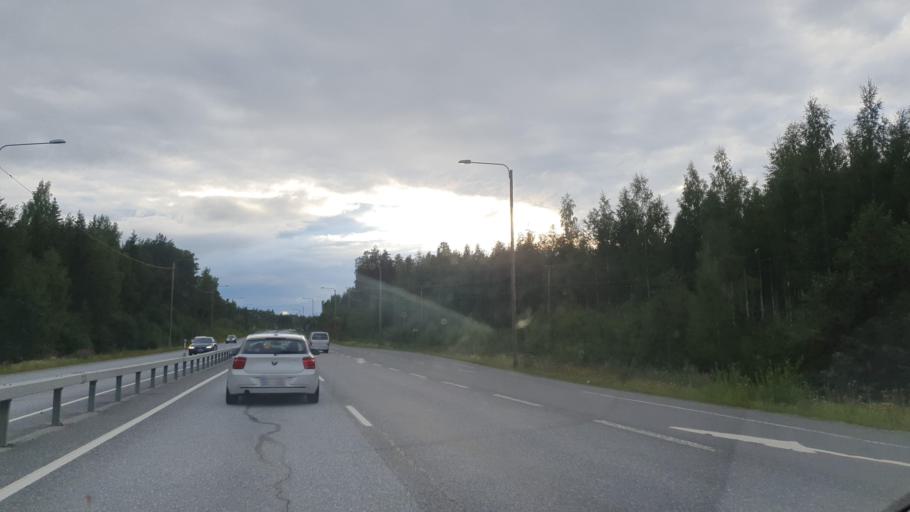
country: FI
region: Southern Savonia
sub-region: Mikkeli
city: Pertunmaa
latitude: 61.4320
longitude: 26.6329
